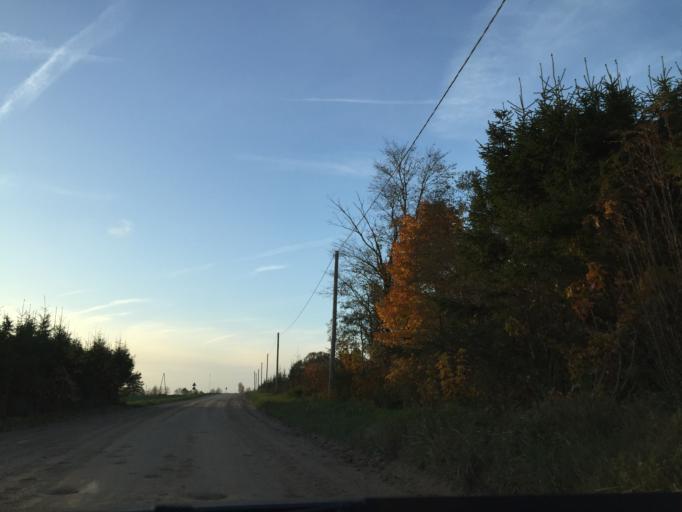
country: LV
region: Malpils
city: Malpils
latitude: 56.8836
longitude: 24.9661
